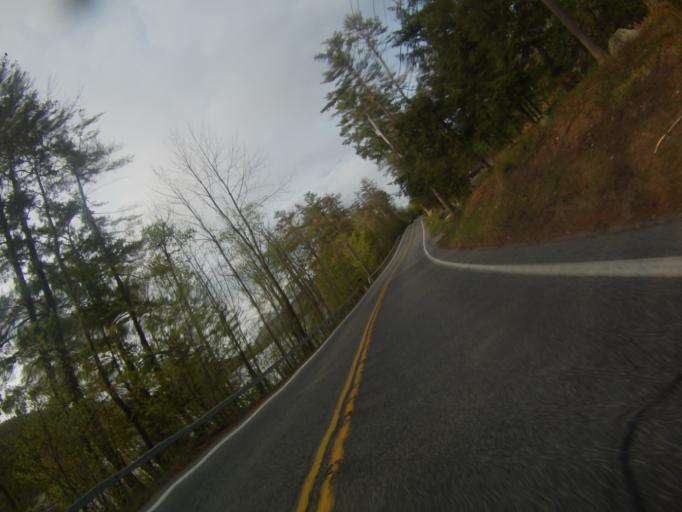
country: US
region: New York
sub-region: Warren County
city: Warrensburg
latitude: 43.7160
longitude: -73.6974
